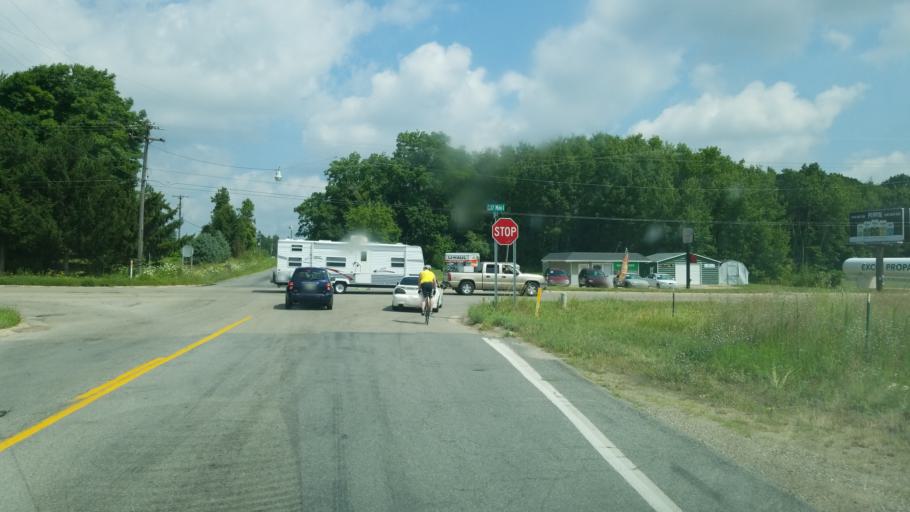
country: US
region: Michigan
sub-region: Kent County
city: Kent City
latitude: 43.2193
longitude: -85.7115
